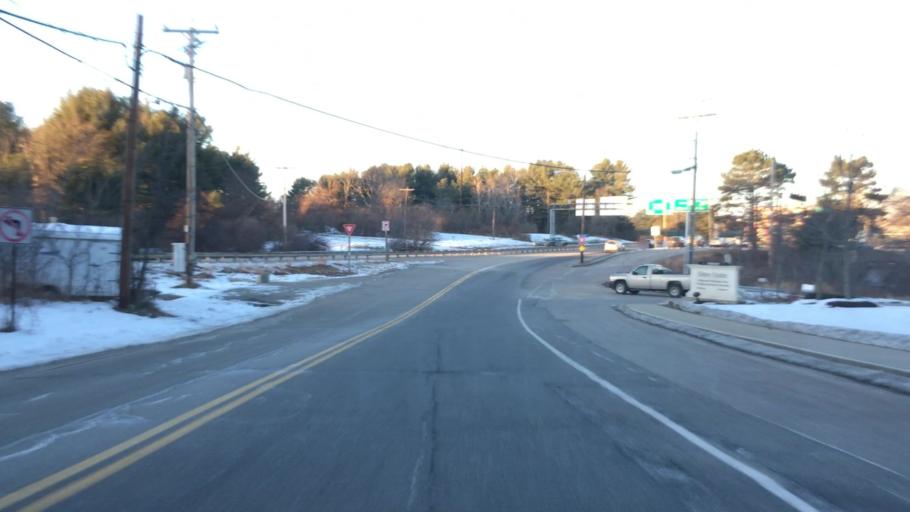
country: US
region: Maine
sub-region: York County
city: Kittery
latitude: 43.1031
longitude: -70.7432
